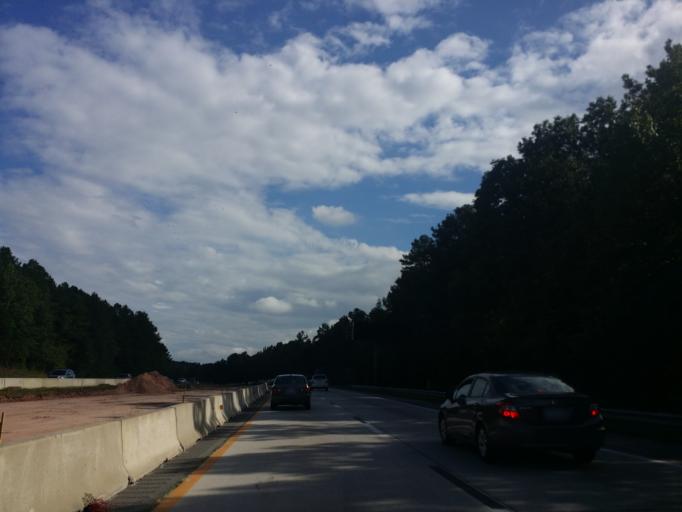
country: US
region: North Carolina
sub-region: Durham County
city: Durham
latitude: 35.9520
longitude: -78.8643
